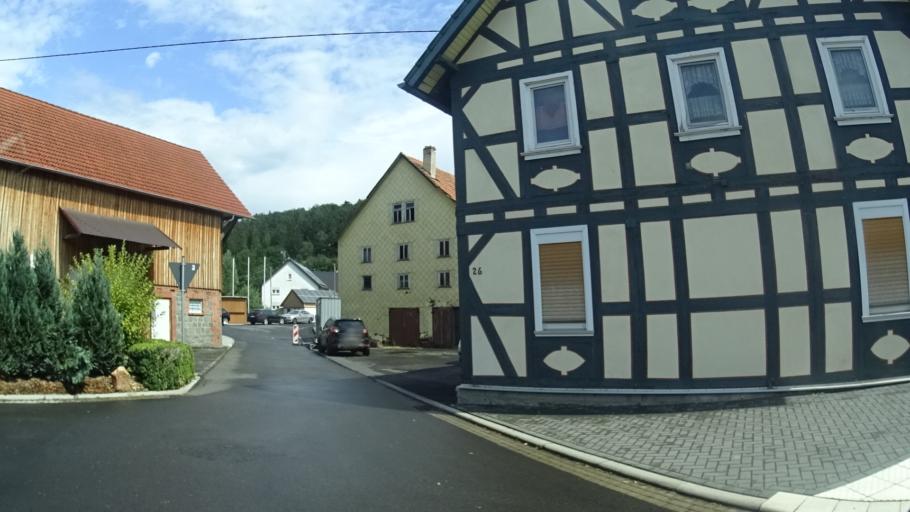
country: DE
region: Hesse
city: Grebenau
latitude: 50.7145
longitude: 9.4474
